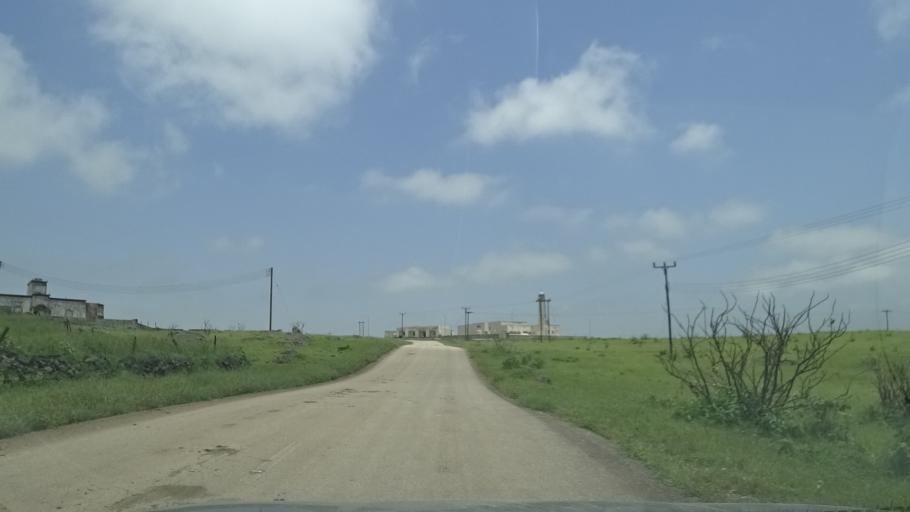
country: OM
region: Zufar
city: Salalah
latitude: 17.2301
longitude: 54.2121
